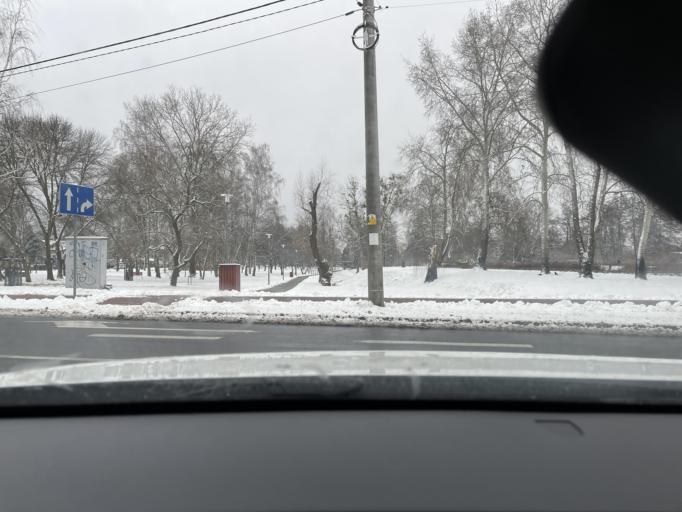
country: PL
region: Masovian Voivodeship
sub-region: Powiat zyrardowski
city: Zyrardow
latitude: 52.0470
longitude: 20.4416
